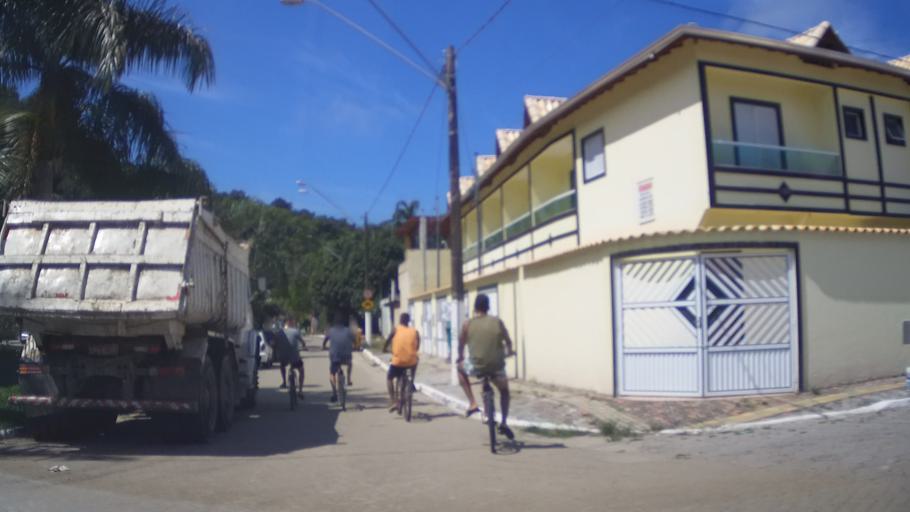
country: BR
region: Sao Paulo
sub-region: Praia Grande
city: Praia Grande
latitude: -24.0086
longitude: -46.3964
